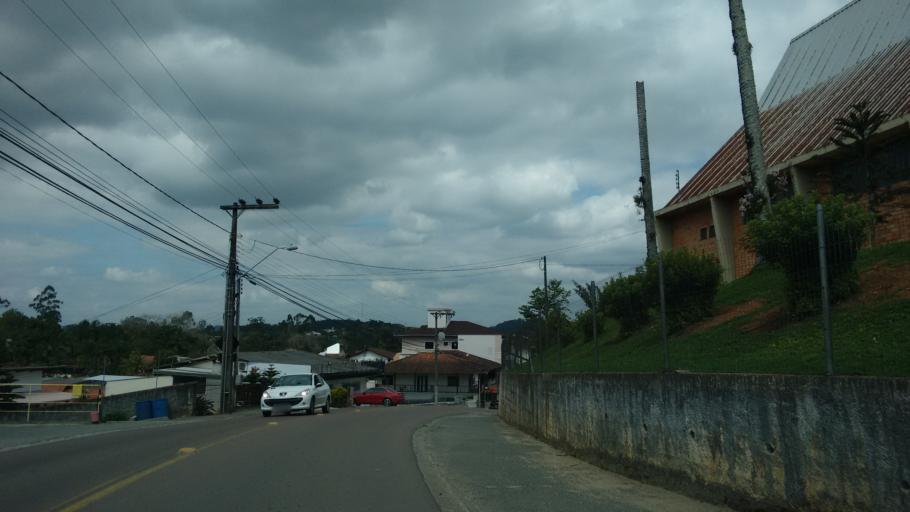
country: BR
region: Santa Catarina
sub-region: Blumenau
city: Blumenau
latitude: -26.8658
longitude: -49.1196
